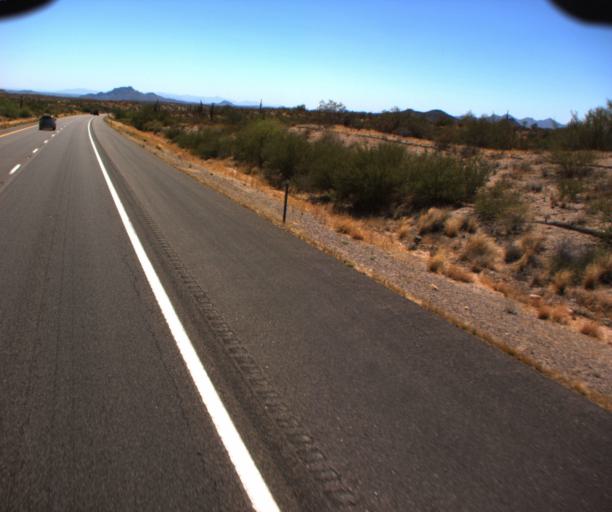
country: US
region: Arizona
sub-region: Maricopa County
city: Rio Verde
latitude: 33.6477
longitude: -111.5321
